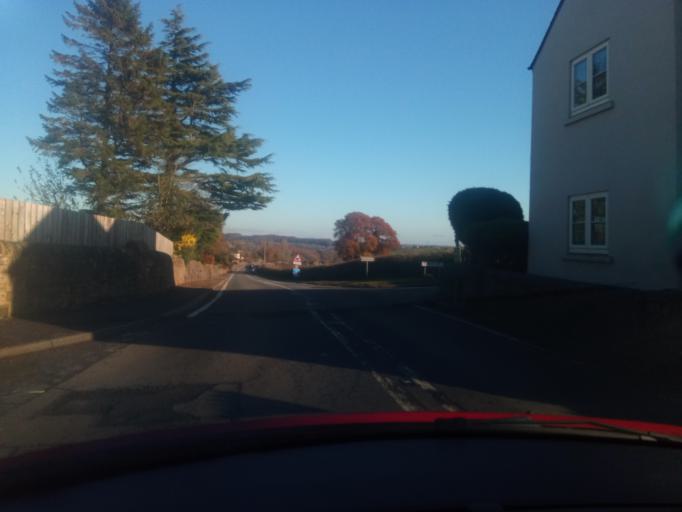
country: GB
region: England
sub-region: Derbyshire
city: Belper
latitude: 53.0212
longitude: -1.5256
